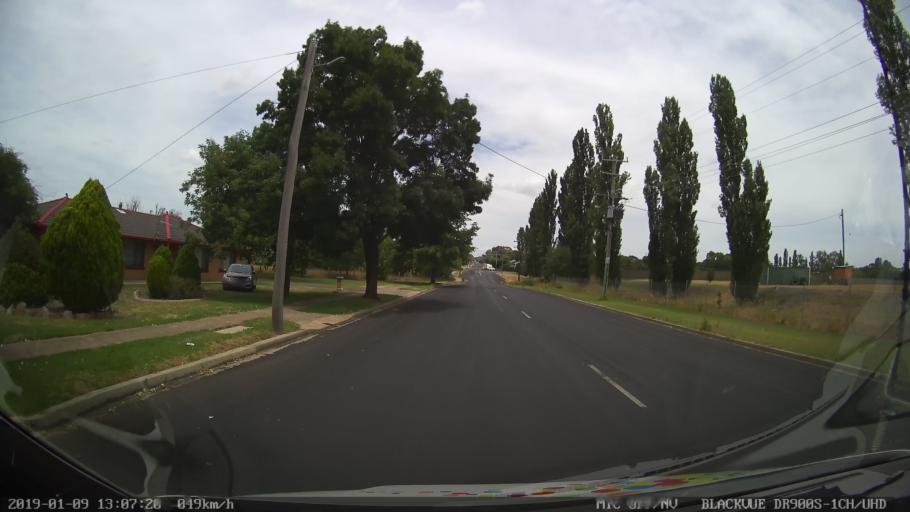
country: AU
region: New South Wales
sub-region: Armidale Dumaresq
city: Armidale
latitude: -30.5190
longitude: 151.6798
